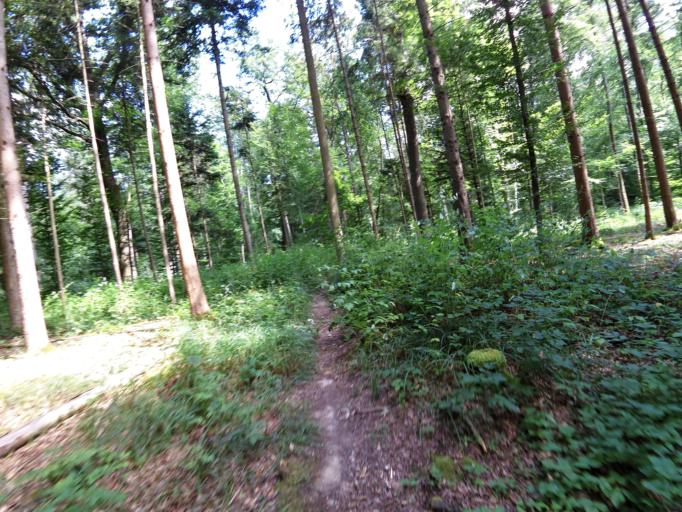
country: CH
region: Thurgau
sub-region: Kreuzlingen District
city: Tagerwilen
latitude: 47.6427
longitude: 9.1076
